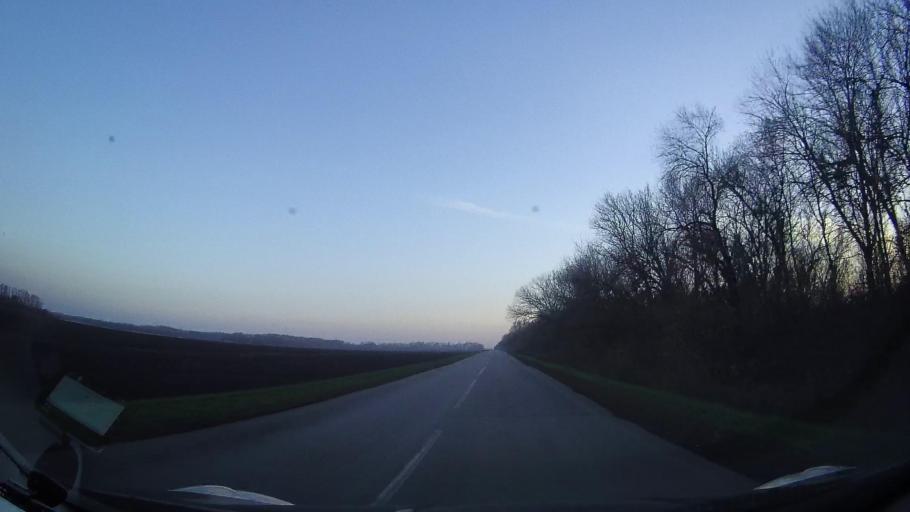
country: RU
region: Rostov
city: Zernograd
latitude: 47.0005
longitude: 40.3915
